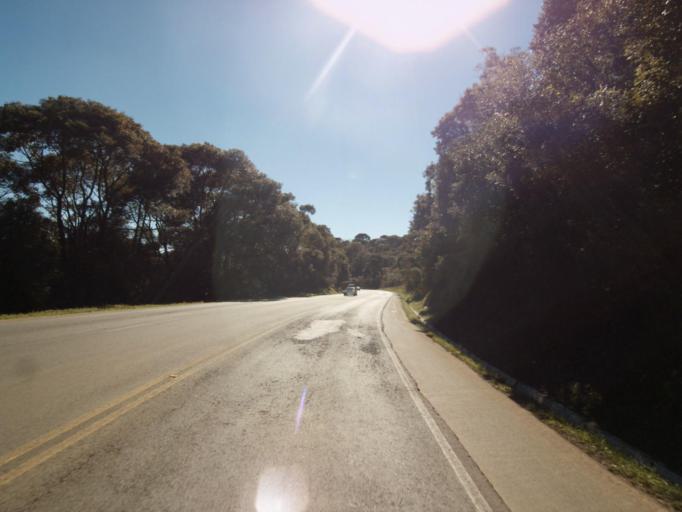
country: BR
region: Santa Catarina
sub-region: Joacaba
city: Joacaba
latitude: -27.0856
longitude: -51.6618
